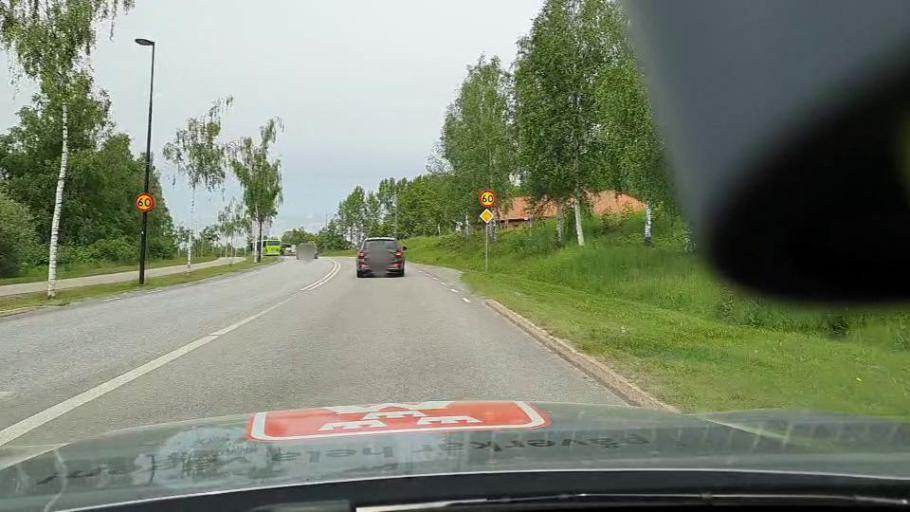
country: SE
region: Soedermanland
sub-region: Flens Kommun
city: Flen
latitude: 59.0627
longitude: 16.5937
